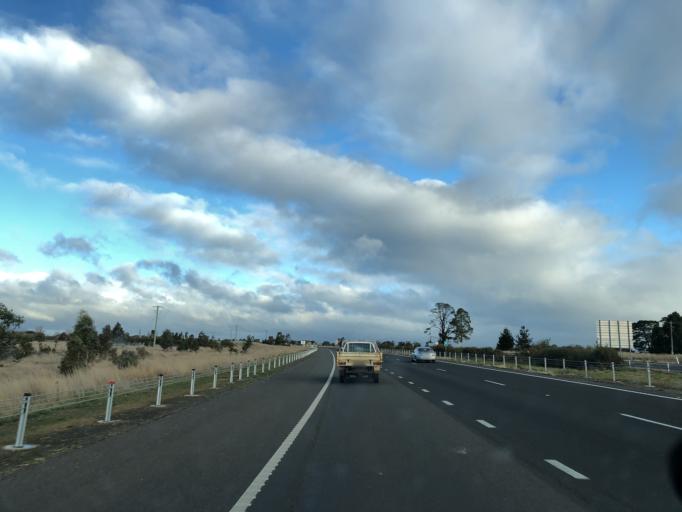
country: AU
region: Victoria
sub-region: Mount Alexander
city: Castlemaine
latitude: -37.1954
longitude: 144.4053
